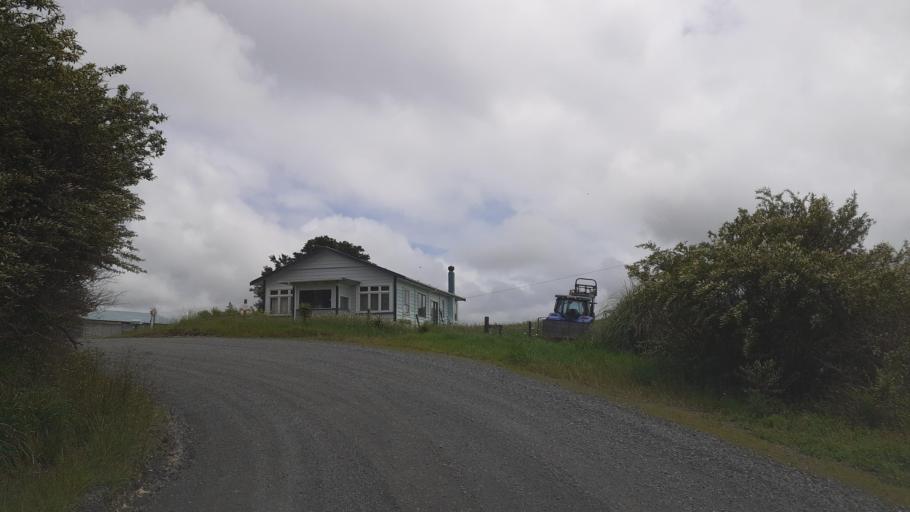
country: NZ
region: Northland
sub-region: Far North District
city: Kawakawa
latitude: -35.5148
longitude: 174.0849
